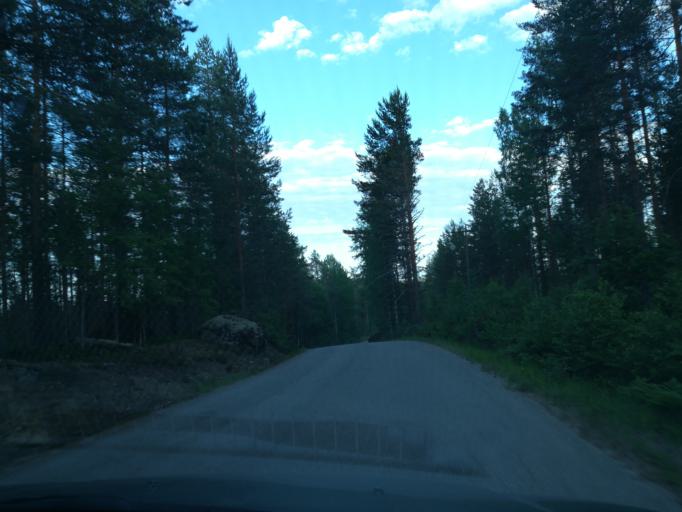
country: FI
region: Southern Savonia
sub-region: Mikkeli
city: Puumala
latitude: 61.5785
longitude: 28.1355
